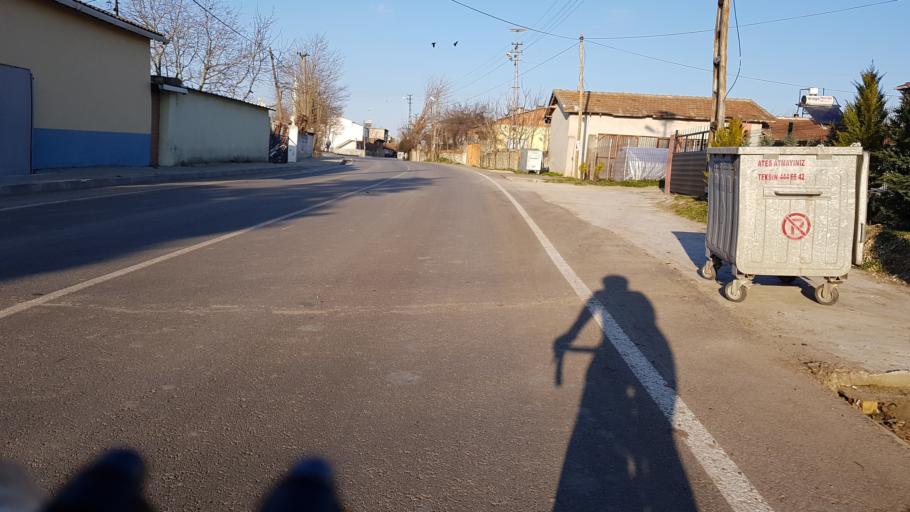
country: TR
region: Tekirdag
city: Beyazkoy
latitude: 41.3037
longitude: 27.7857
